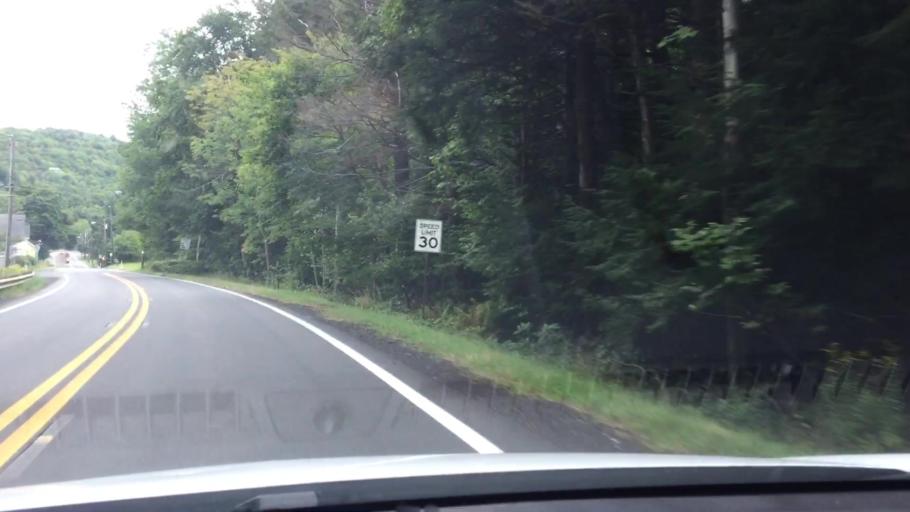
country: US
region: Massachusetts
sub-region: Berkshire County
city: Becket
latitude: 42.3340
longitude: -73.0873
